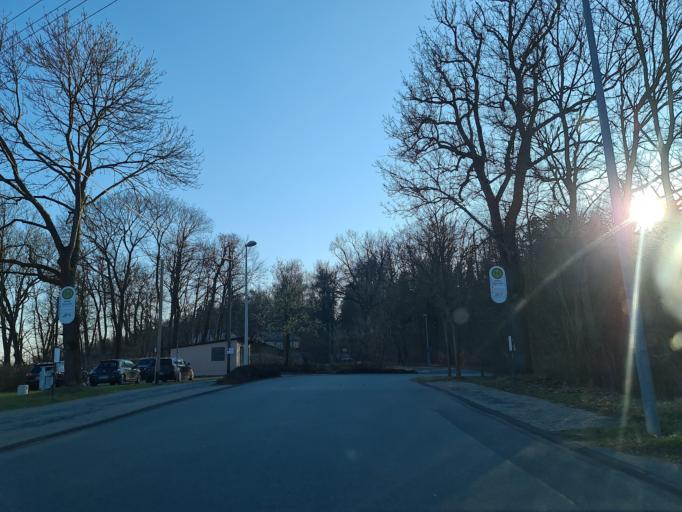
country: DE
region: Saxony
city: Plauen
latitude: 50.5293
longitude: 12.1477
